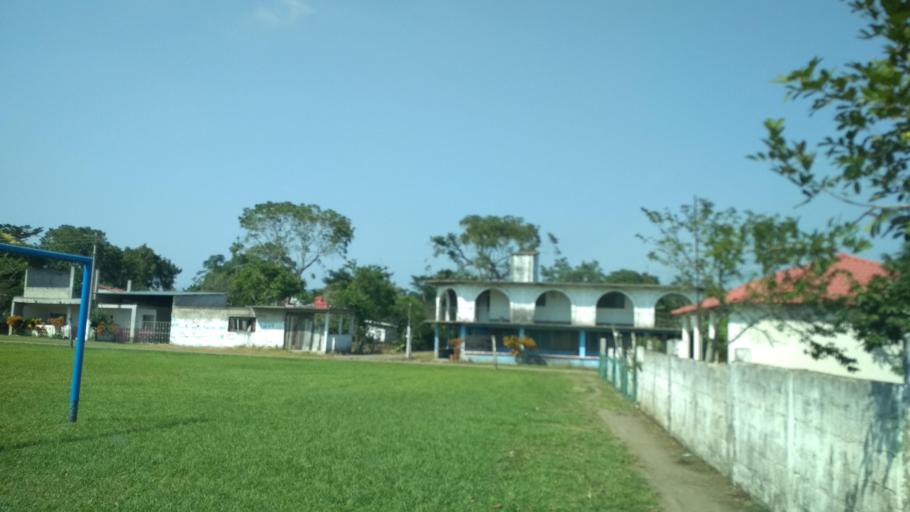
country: MX
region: Puebla
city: San Jose Acateno
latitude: 20.1739
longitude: -97.1975
